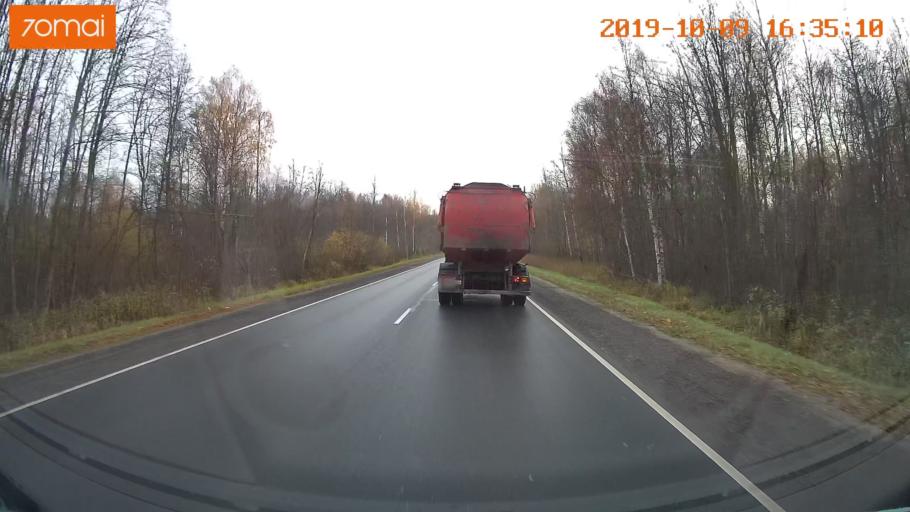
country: RU
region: Kostroma
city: Oktyabr'skiy
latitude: 57.5585
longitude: 40.9984
